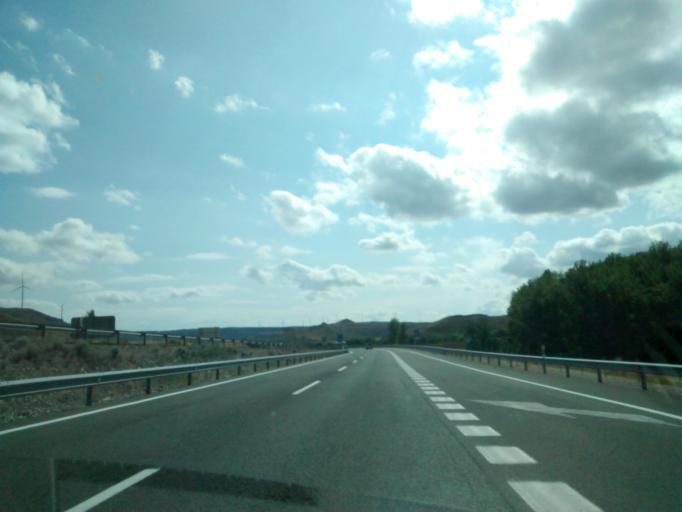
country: ES
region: Castille and Leon
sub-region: Provincia de Soria
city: Medinaceli
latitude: 41.1559
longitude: -2.4224
